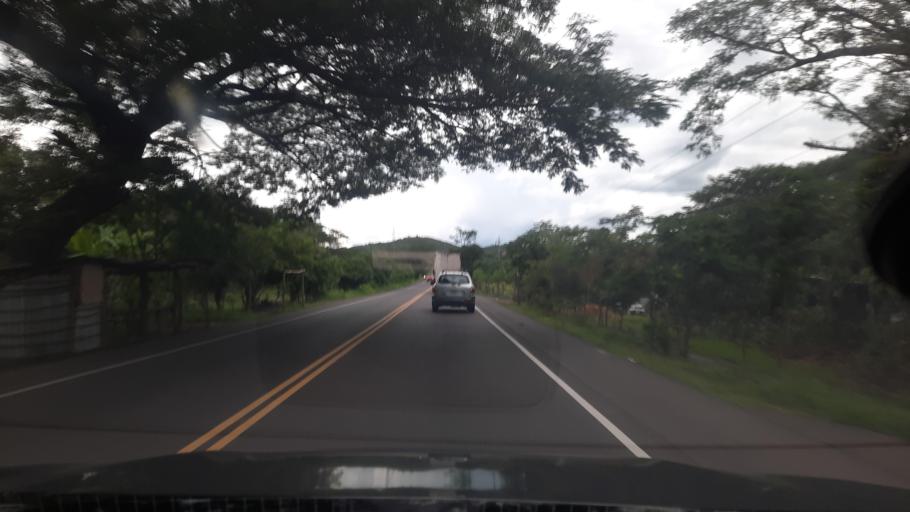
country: HN
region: Choluteca
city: Marcovia
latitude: 13.3712
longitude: -87.2962
